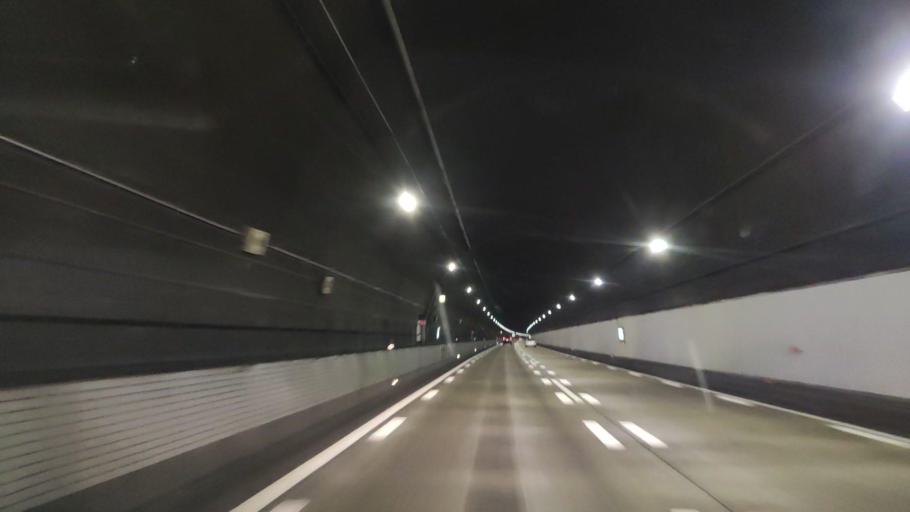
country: JP
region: Hiroshima
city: Fukuyama
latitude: 34.4985
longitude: 133.3201
